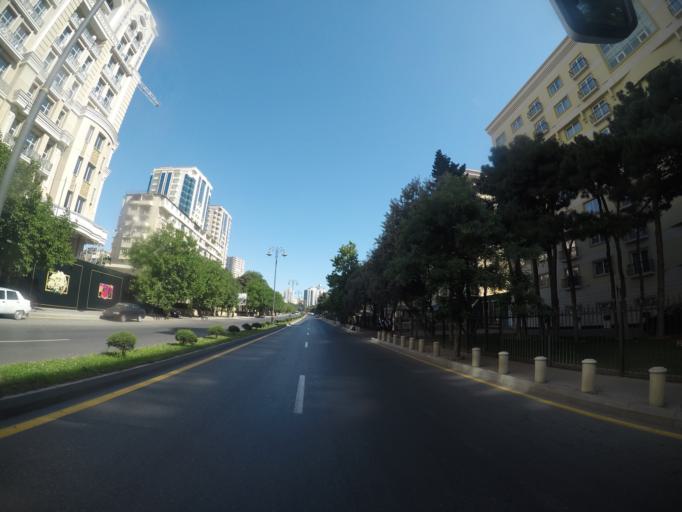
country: AZ
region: Baki
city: Badamdar
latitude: 40.3876
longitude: 49.8240
